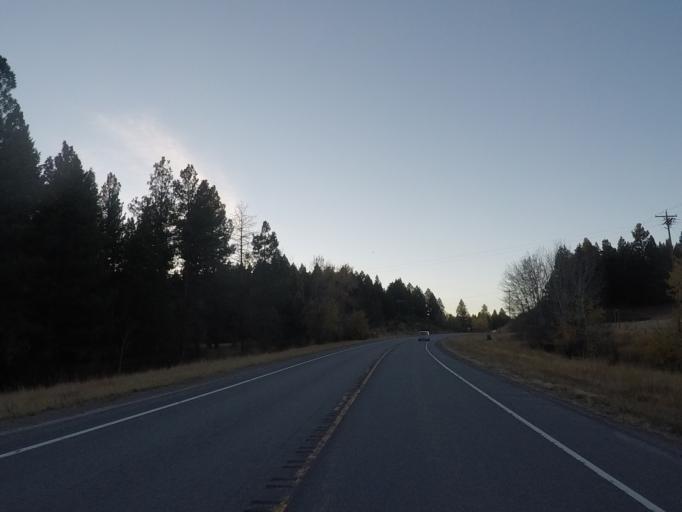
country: US
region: Montana
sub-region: Lewis and Clark County
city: Lincoln
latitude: 47.0083
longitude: -113.0552
